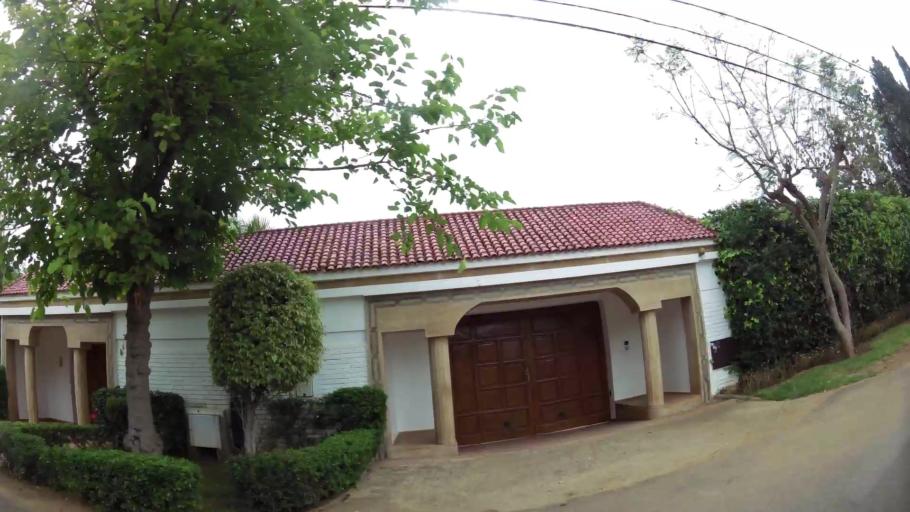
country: MA
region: Rabat-Sale-Zemmour-Zaer
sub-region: Rabat
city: Rabat
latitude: 33.9659
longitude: -6.8154
